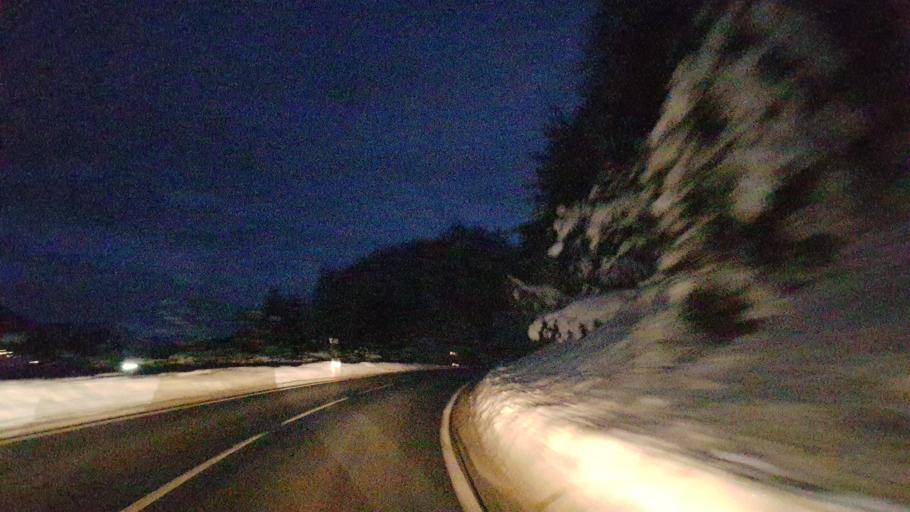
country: AT
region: Salzburg
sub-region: Politischer Bezirk Sankt Johann im Pongau
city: Forstau
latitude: 47.3829
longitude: 13.5022
